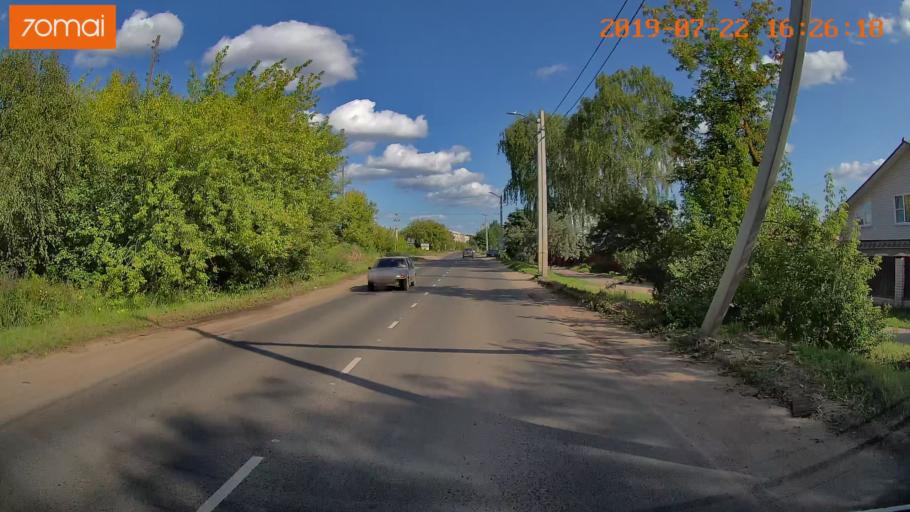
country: RU
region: Ivanovo
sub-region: Gorod Ivanovo
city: Ivanovo
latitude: 57.0497
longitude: 40.9326
